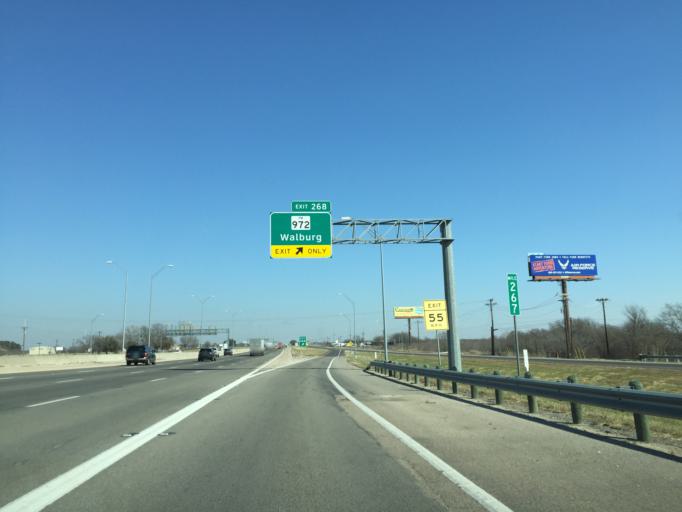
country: US
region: Texas
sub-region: Williamson County
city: Serenada
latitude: 30.7072
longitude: -97.6497
